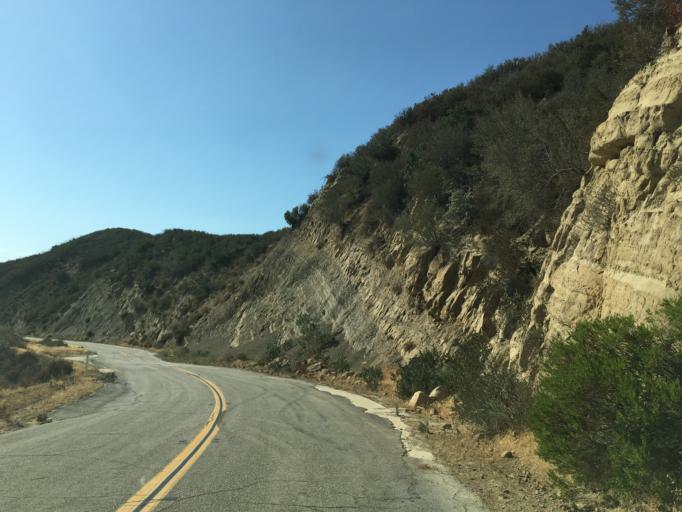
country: US
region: California
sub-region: Los Angeles County
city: Castaic
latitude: 34.5748
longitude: -118.6689
